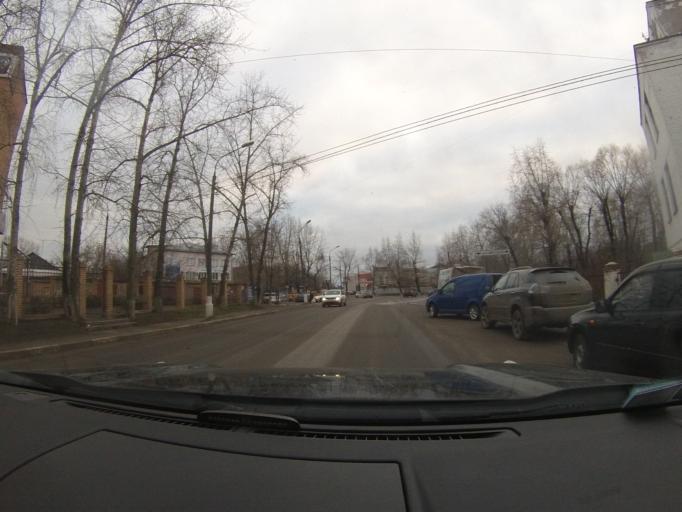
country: RU
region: Moskovskaya
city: Voskresensk
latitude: 55.3185
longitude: 38.6848
